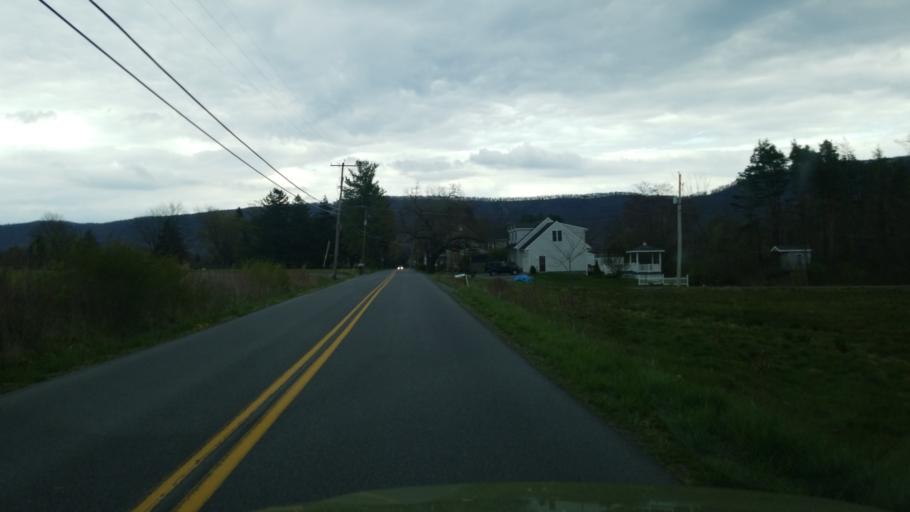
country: US
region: Pennsylvania
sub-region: Blair County
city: Tipton
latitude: 40.6404
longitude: -78.3033
